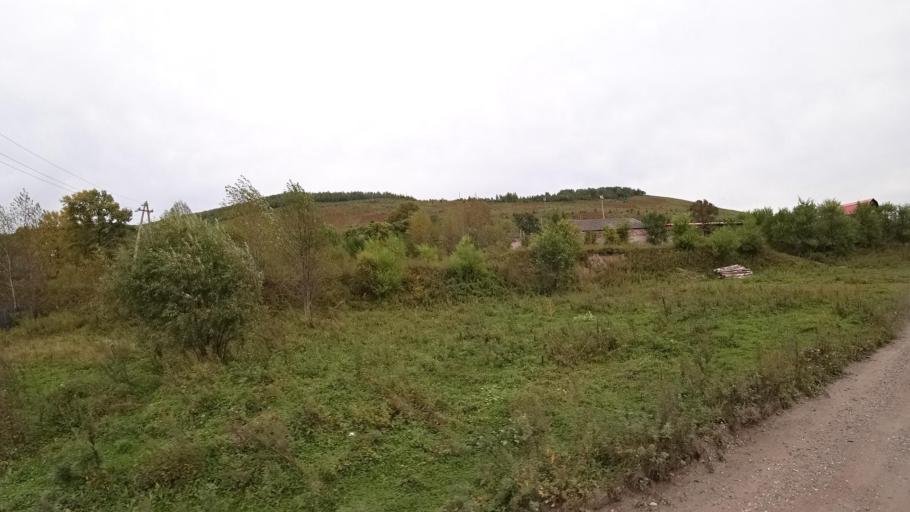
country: RU
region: Jewish Autonomous Oblast
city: Khingansk
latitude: 49.0317
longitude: 131.0565
